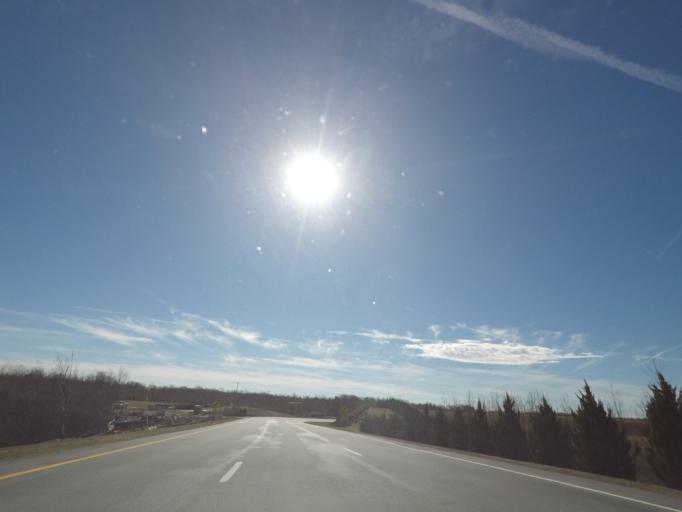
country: US
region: North Carolina
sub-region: Guilford County
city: Oak Ridge
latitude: 36.1202
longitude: -79.9344
